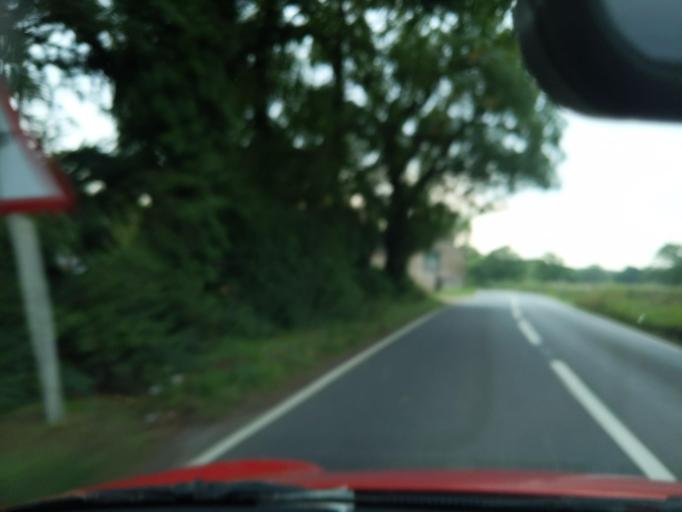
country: GB
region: England
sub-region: Devon
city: Okehampton
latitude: 50.8124
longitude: -4.0653
